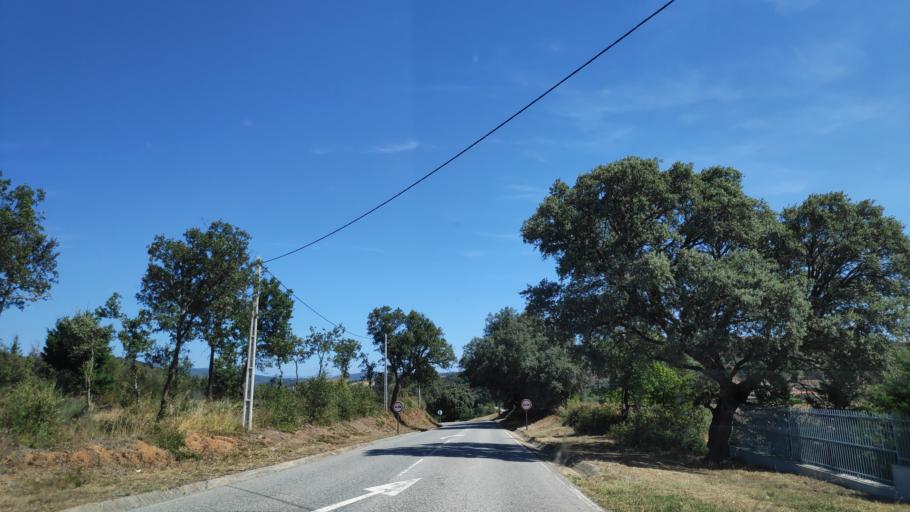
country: PT
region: Braganca
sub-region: Braganca Municipality
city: Braganca
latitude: 41.8256
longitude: -6.7493
